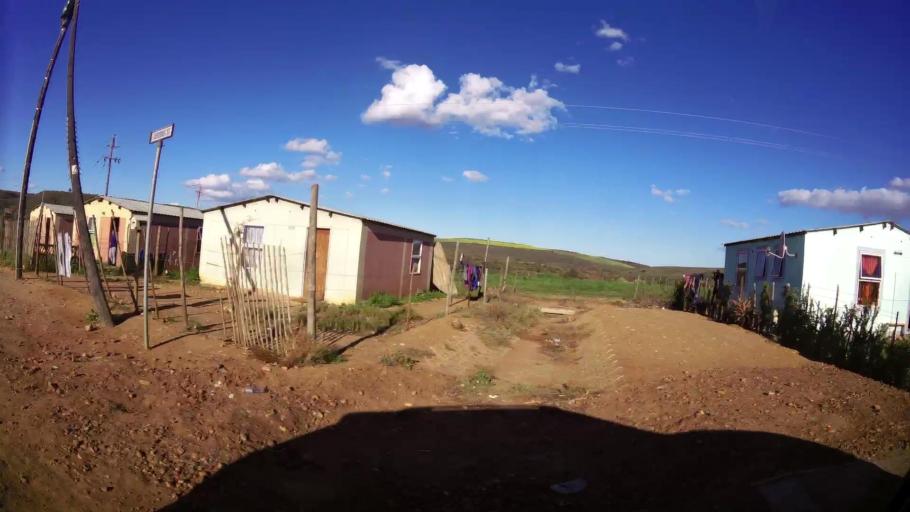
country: ZA
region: Western Cape
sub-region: Eden District Municipality
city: Riversdale
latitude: -34.1093
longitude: 20.9661
